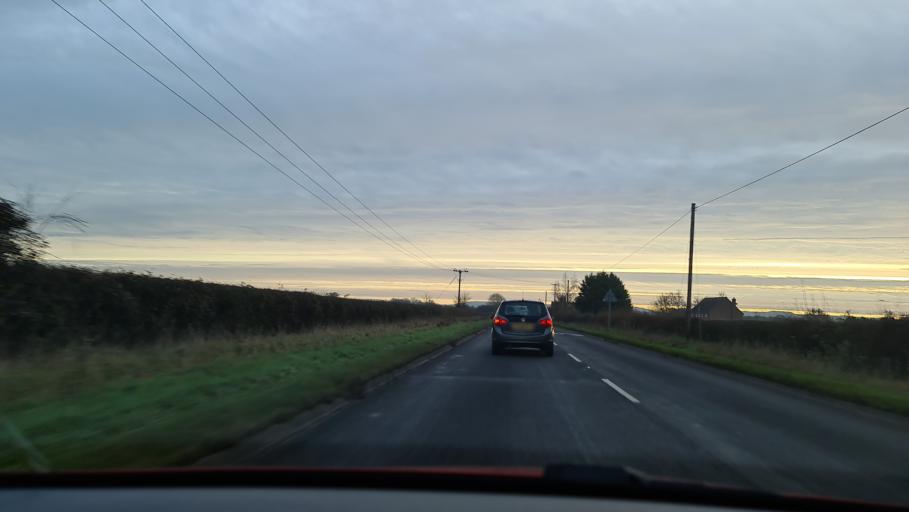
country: GB
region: England
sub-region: Buckinghamshire
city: Haddenham
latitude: 51.7543
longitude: -0.9139
